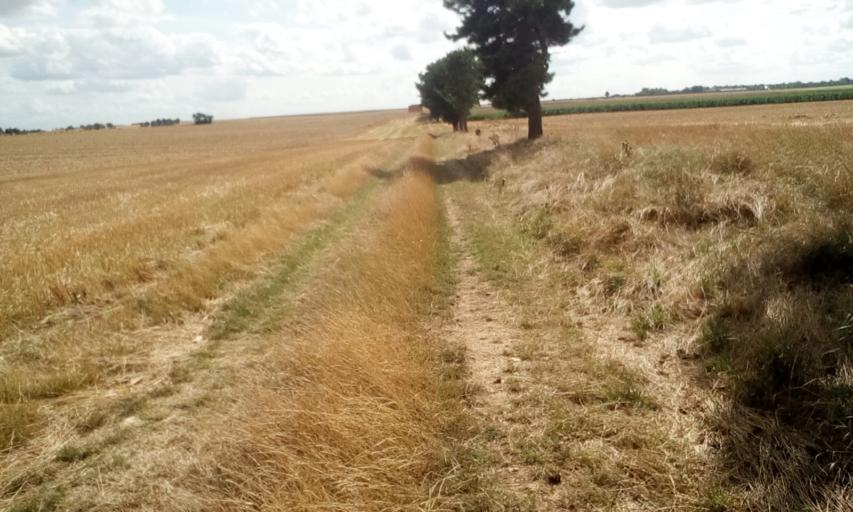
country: FR
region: Lower Normandy
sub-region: Departement du Calvados
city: Bellengreville
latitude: 49.0937
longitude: -0.2029
